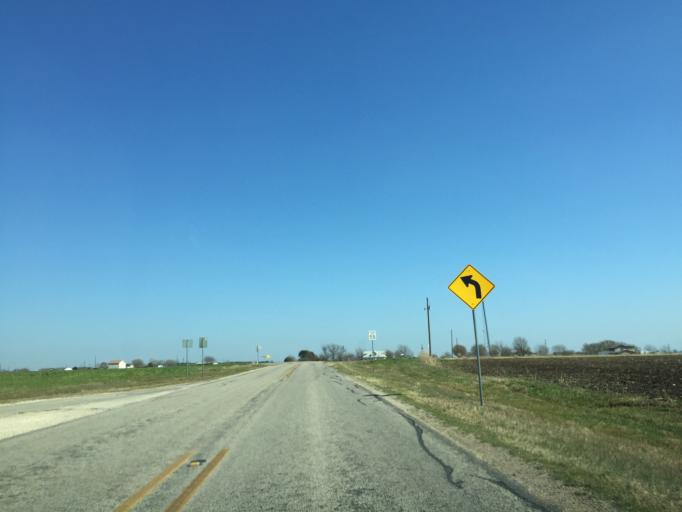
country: US
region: Texas
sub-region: Williamson County
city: Georgetown
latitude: 30.6865
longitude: -97.5879
